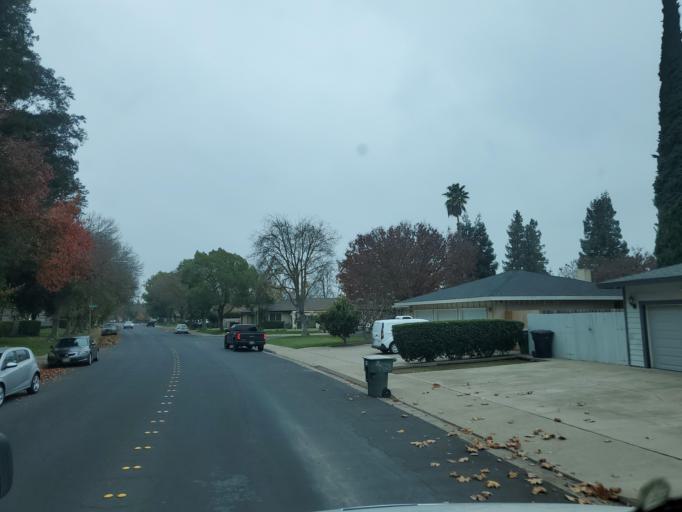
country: US
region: California
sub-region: Stanislaus County
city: Modesto
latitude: 37.6812
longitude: -120.9985
